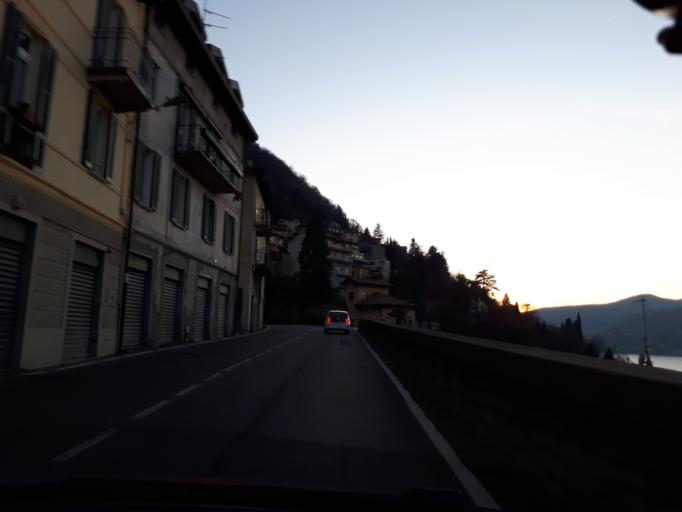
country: IT
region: Lombardy
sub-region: Provincia di Como
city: Blevio
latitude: 45.8370
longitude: 9.1019
